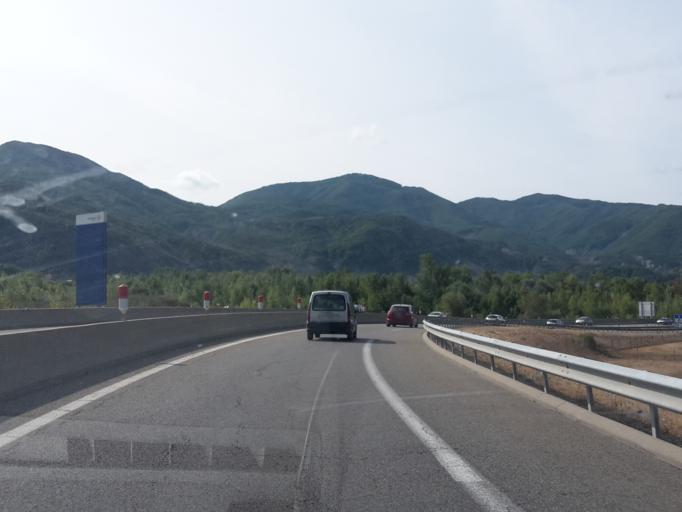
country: FR
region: Provence-Alpes-Cote d'Azur
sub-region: Departement des Hautes-Alpes
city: Tallard
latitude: 44.4393
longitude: 6.0292
